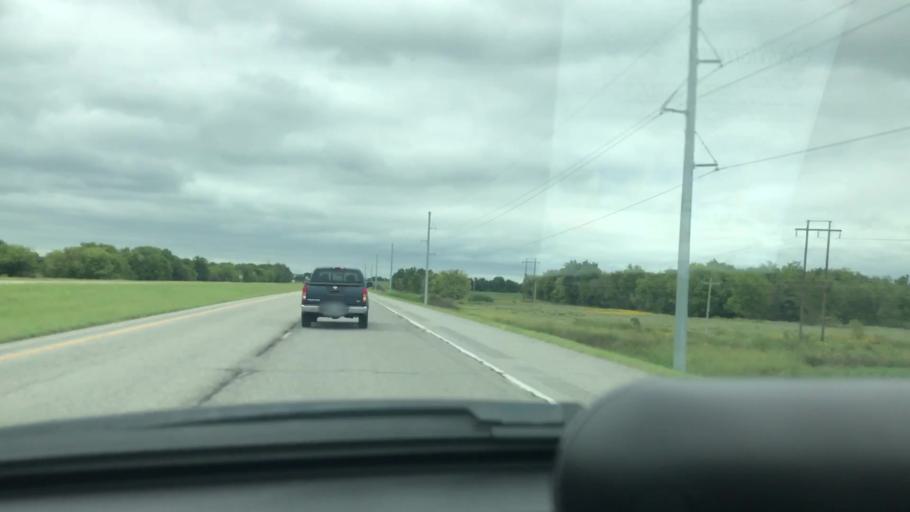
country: US
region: Oklahoma
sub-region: Wagoner County
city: Wagoner
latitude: 36.0004
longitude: -95.3689
